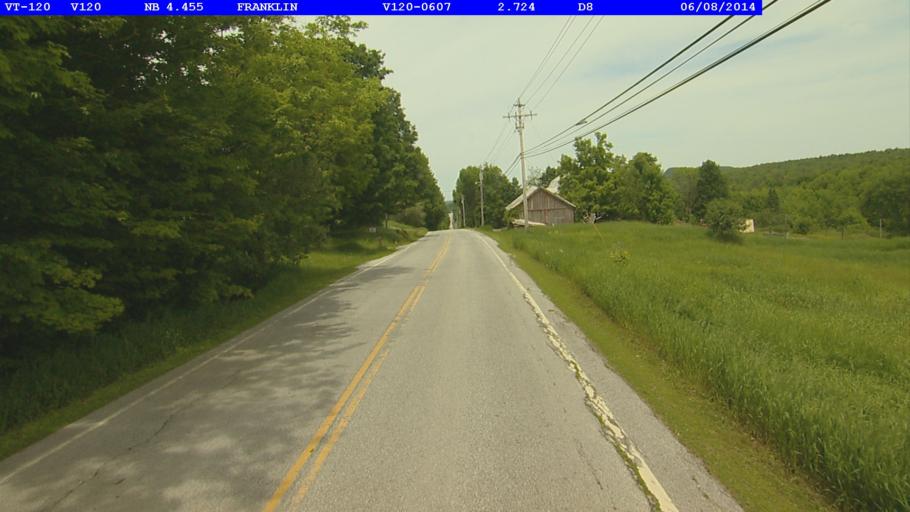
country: US
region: Vermont
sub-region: Franklin County
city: Enosburg Falls
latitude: 44.9719
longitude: -72.9104
